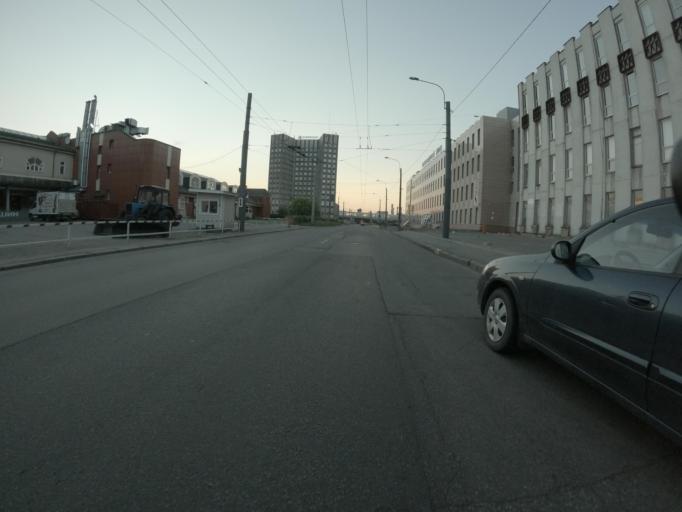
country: RU
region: St.-Petersburg
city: Avtovo
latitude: 59.8528
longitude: 30.2830
